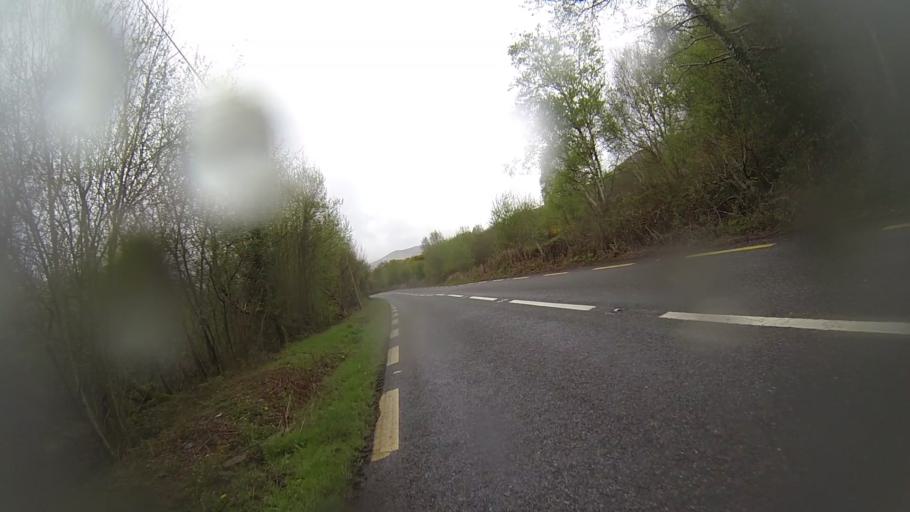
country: IE
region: Munster
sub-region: Ciarrai
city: Kenmare
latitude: 51.8132
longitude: -9.5479
